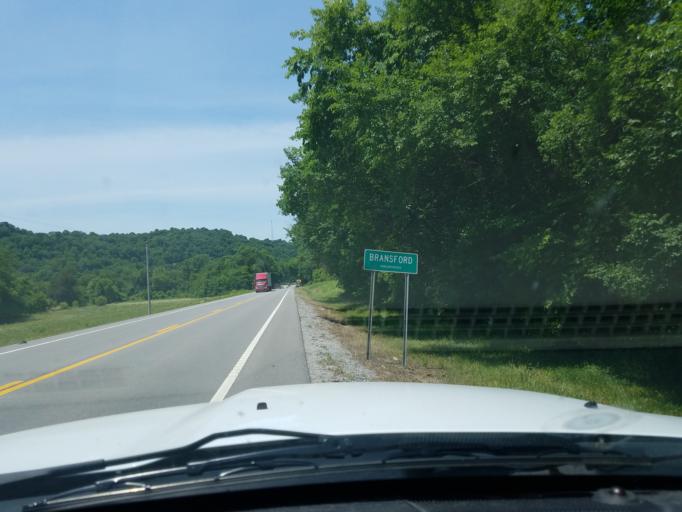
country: US
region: Tennessee
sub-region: Sumner County
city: Westmoreland
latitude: 36.4963
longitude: -86.2759
